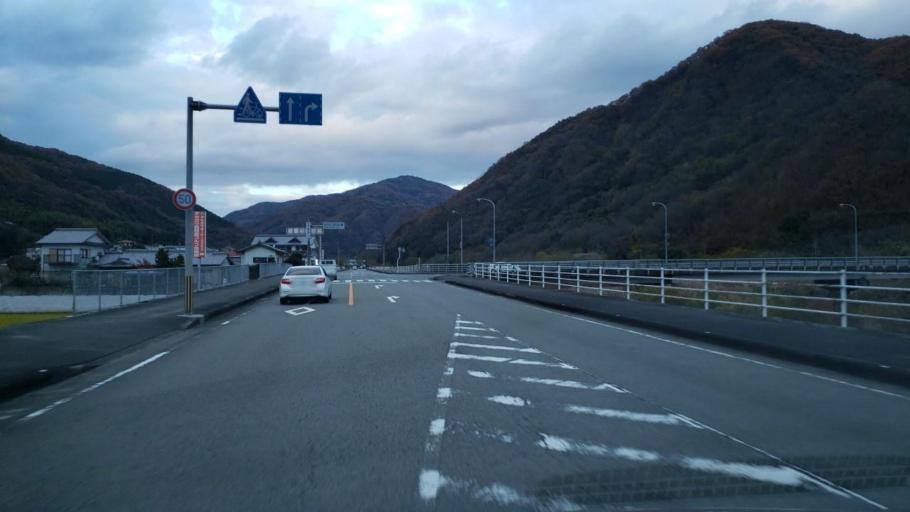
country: JP
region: Tokushima
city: Wakimachi
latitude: 34.0901
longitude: 134.1730
